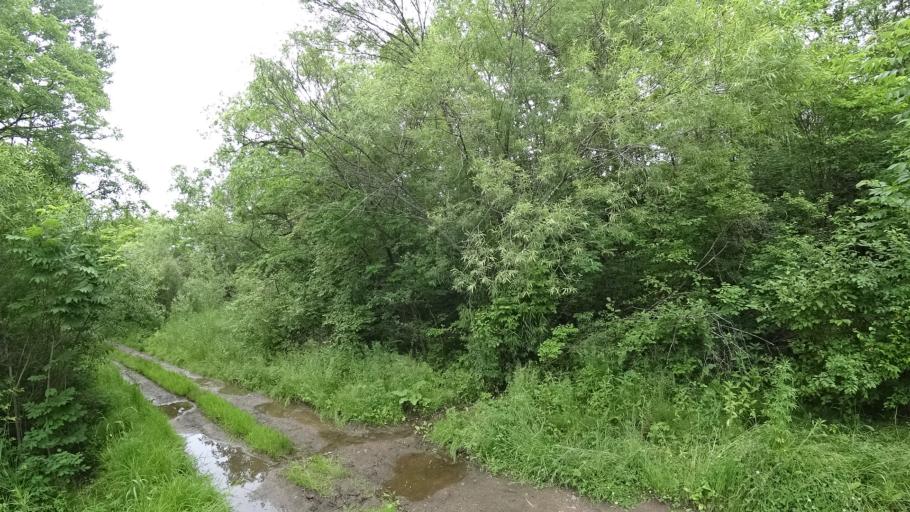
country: RU
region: Primorskiy
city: Novosysoyevka
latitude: 44.2037
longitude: 133.3282
